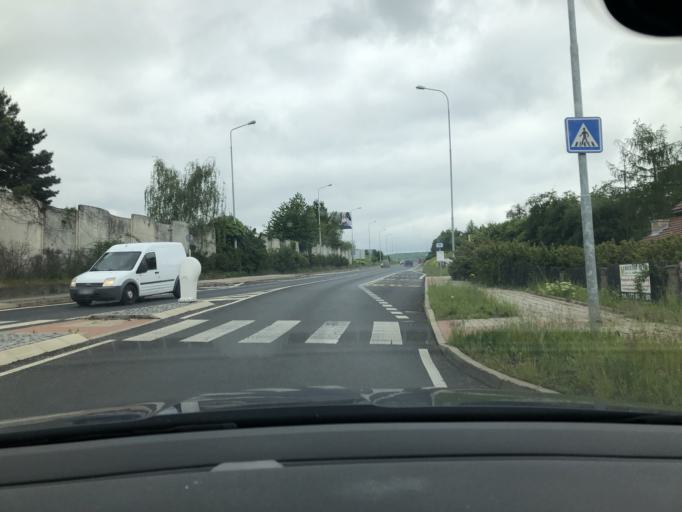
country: CZ
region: Ustecky
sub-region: Okres Usti nad Labem
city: Usti nad Labem
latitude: 50.6891
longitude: 14.0184
